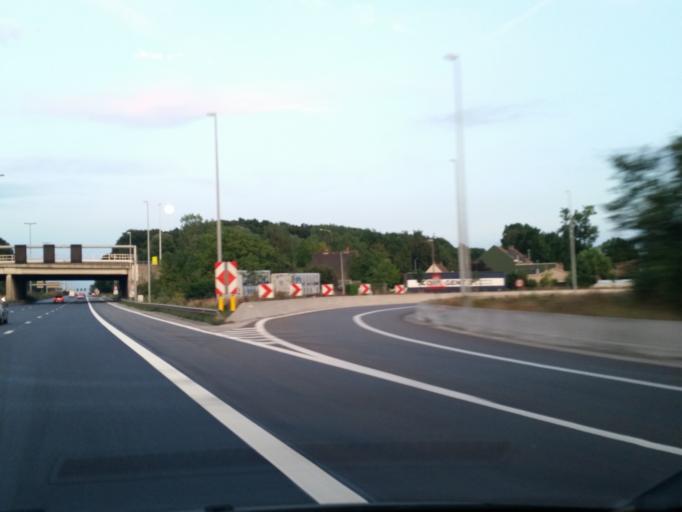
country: BE
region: Flanders
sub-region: Provincie Oost-Vlaanderen
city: Merelbeke
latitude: 50.9997
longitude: 3.7683
